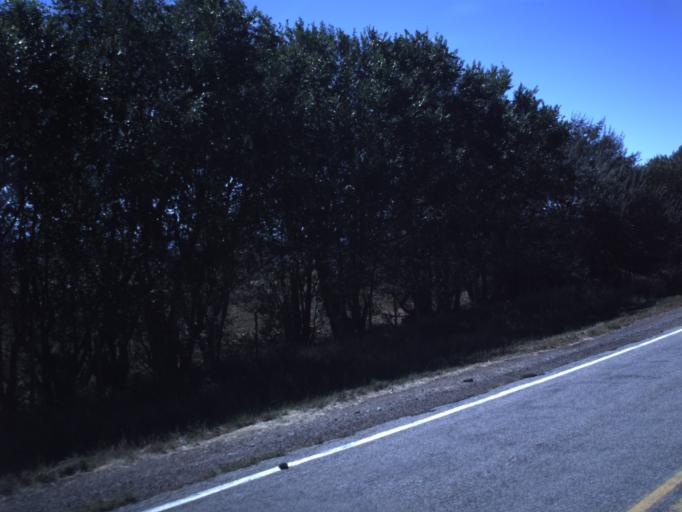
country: US
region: Utah
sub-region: Grand County
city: Moab
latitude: 38.3124
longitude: -109.2519
